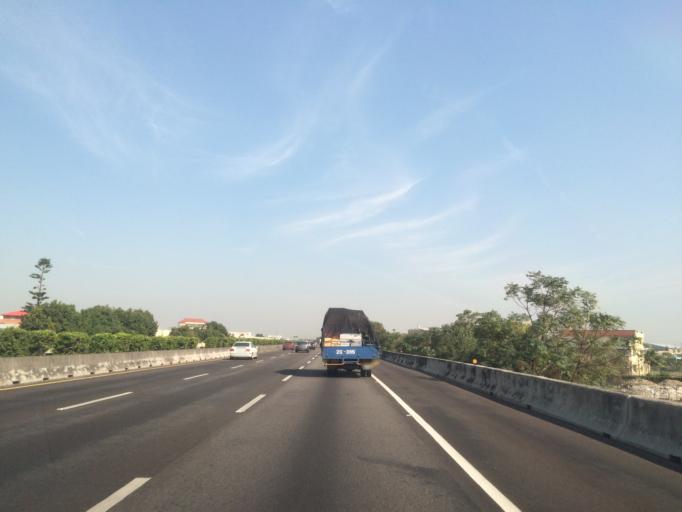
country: TW
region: Taiwan
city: Fengyuan
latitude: 24.2316
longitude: 120.6868
